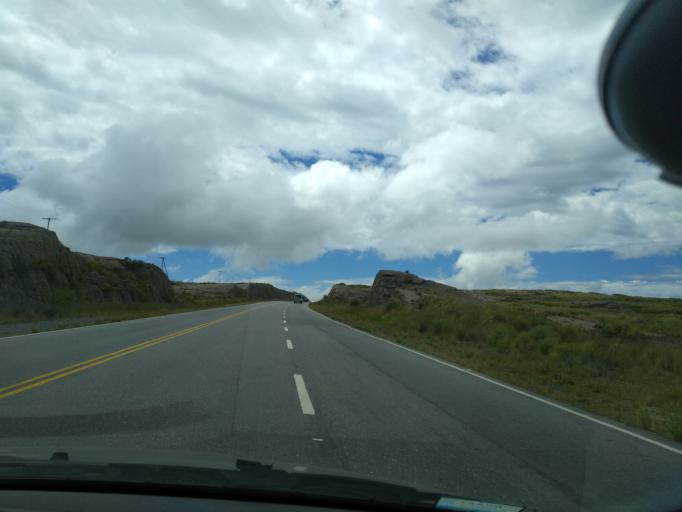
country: AR
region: Cordoba
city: Mina Clavero
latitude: -31.6100
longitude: -64.8322
